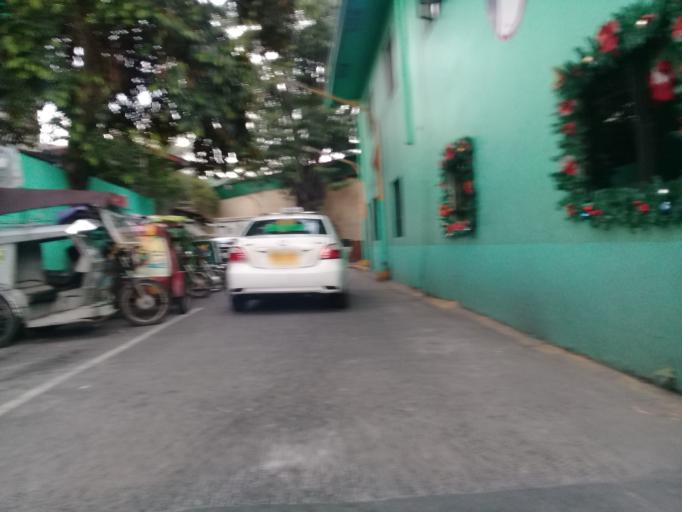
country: PH
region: Metro Manila
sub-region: Mandaluyong
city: Mandaluyong City
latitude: 14.5793
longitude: 121.0159
